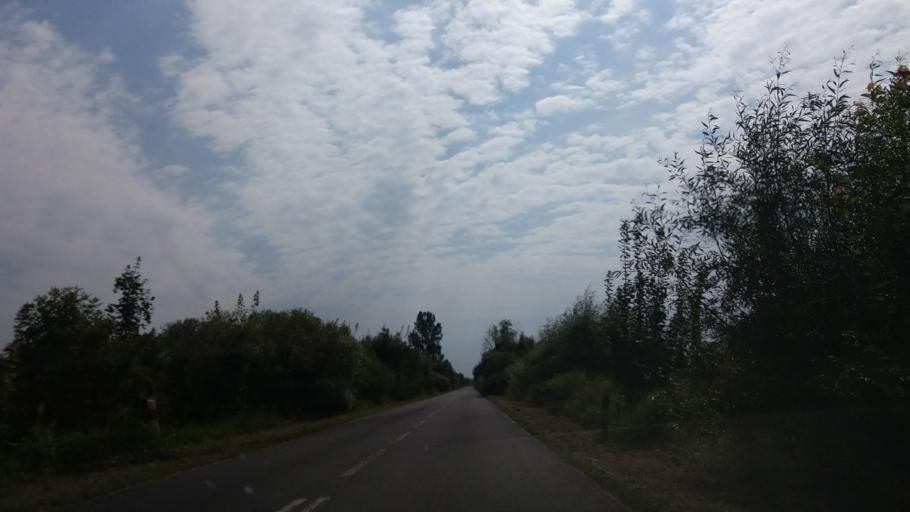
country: PL
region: Lubusz
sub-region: Powiat strzelecko-drezdenecki
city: Stare Kurowo
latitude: 52.8089
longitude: 15.6373
